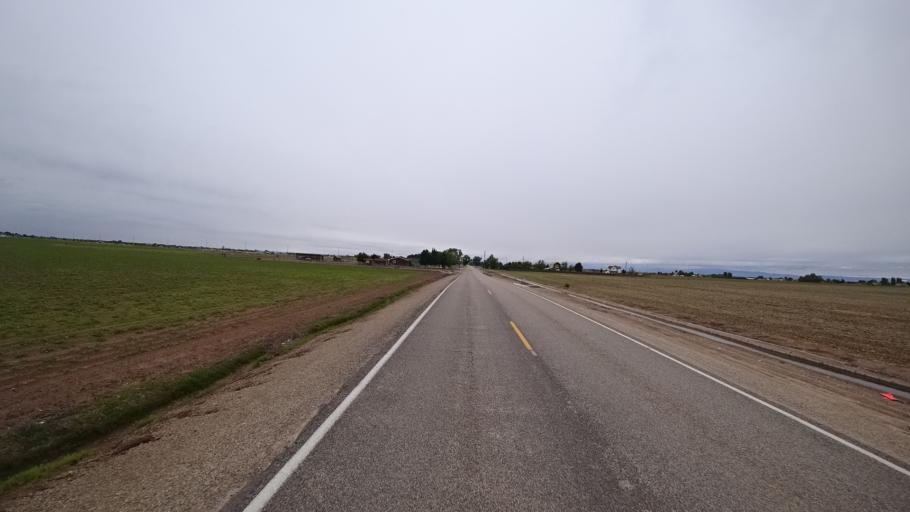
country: US
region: Idaho
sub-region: Ada County
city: Star
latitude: 43.6582
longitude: -116.4734
